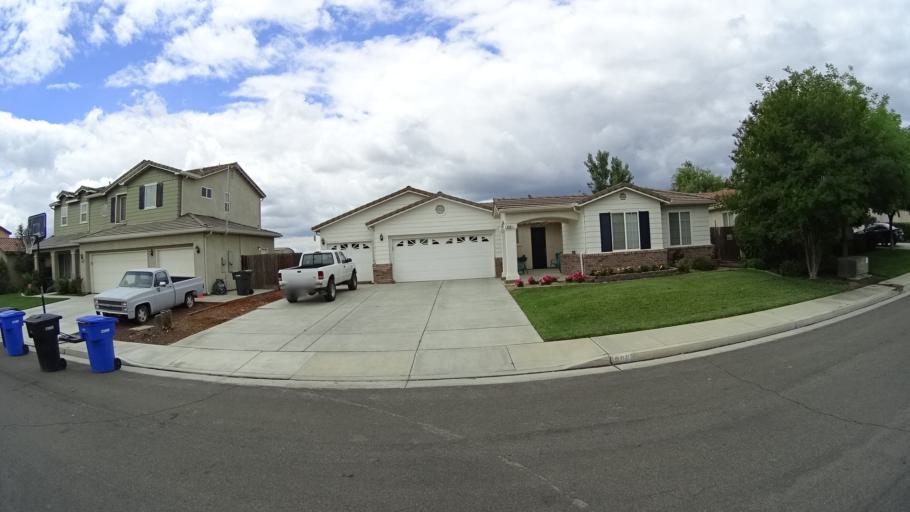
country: US
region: California
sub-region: Kings County
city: Armona
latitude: 36.3320
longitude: -119.6837
